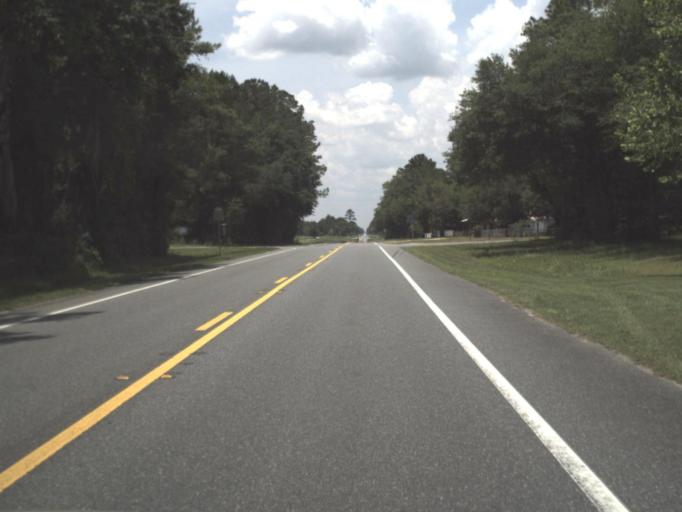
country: US
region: Florida
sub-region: Columbia County
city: Watertown
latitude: 30.1072
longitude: -82.4903
